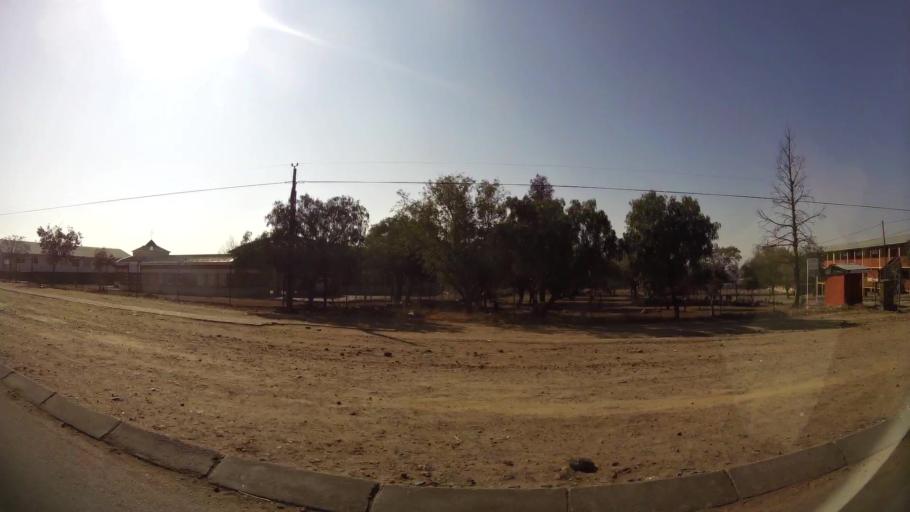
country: ZA
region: Orange Free State
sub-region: Mangaung Metropolitan Municipality
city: Bloemfontein
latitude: -29.1773
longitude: 26.2418
